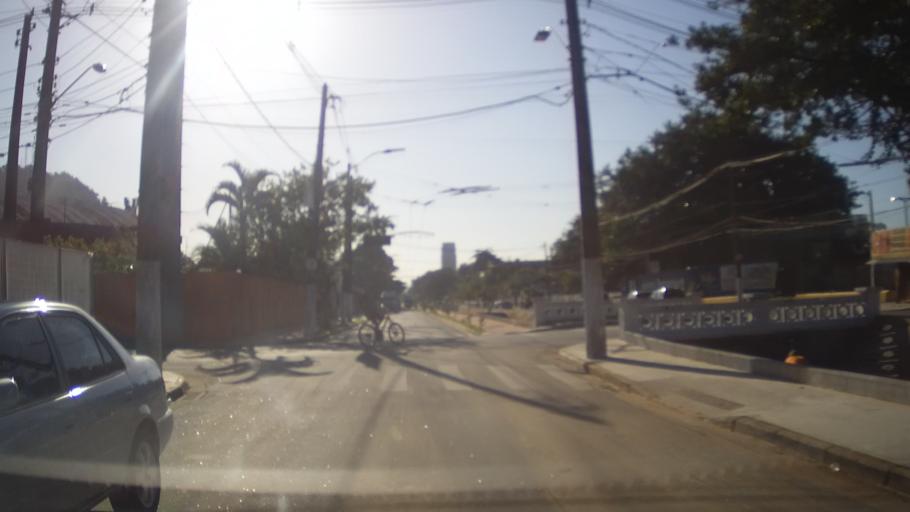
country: BR
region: Sao Paulo
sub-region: Santos
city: Santos
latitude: -23.9426
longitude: -46.3400
